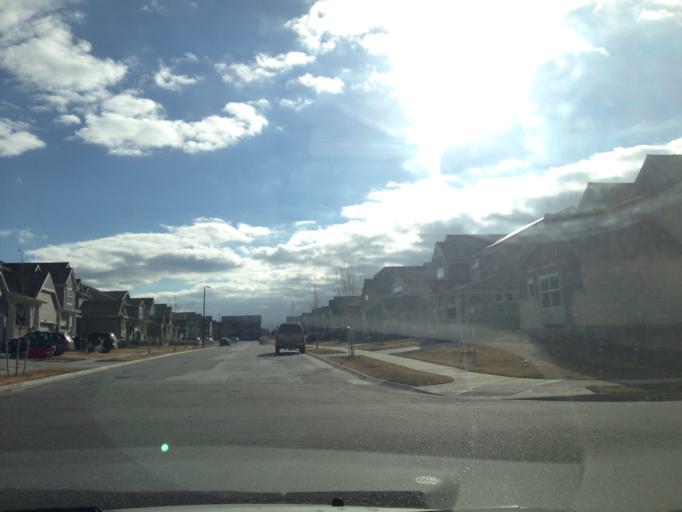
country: US
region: Colorado
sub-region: Boulder County
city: Lafayette
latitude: 40.0320
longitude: -105.0888
